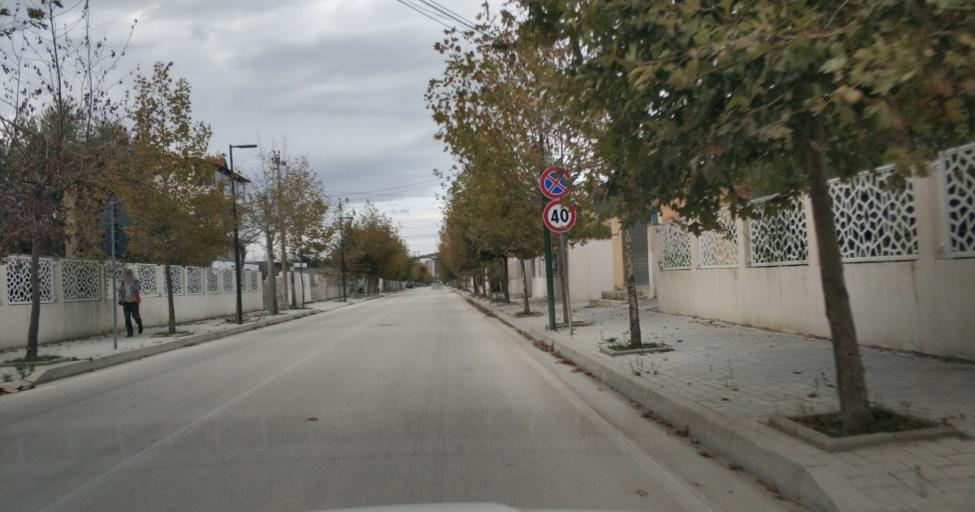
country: AL
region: Vlore
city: Vlore
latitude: 40.4480
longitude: 19.4968
